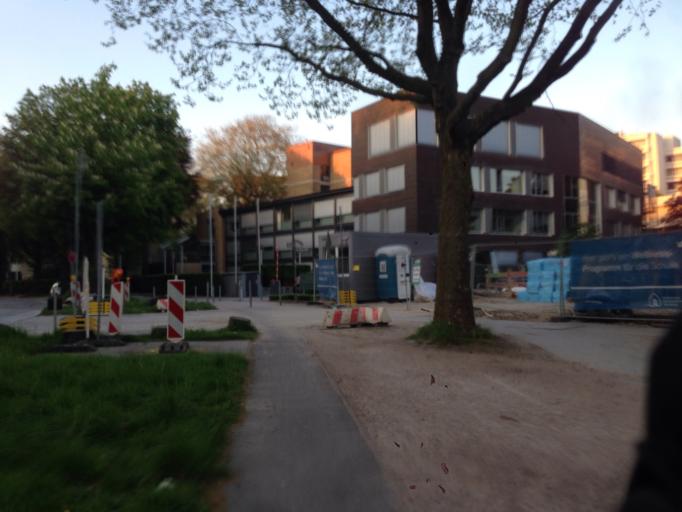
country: DE
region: Hamburg
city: Eimsbuettel
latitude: 53.5624
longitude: 9.9936
